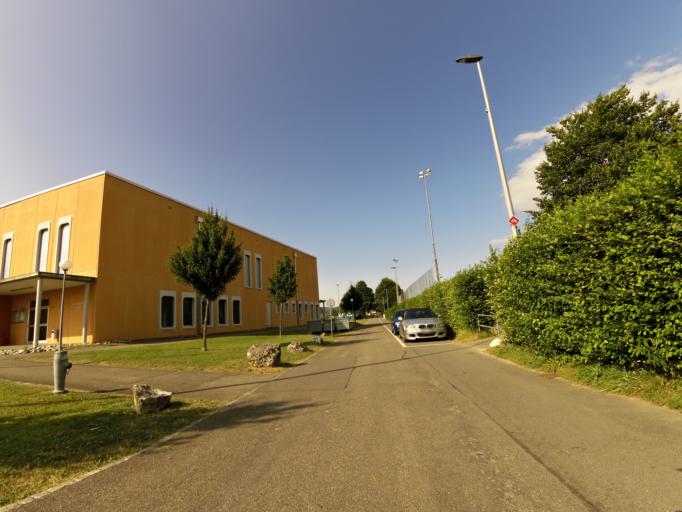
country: CH
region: Solothurn
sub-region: Bezirk Olten
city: Niedergosgen
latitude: 47.3656
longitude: 7.9906
